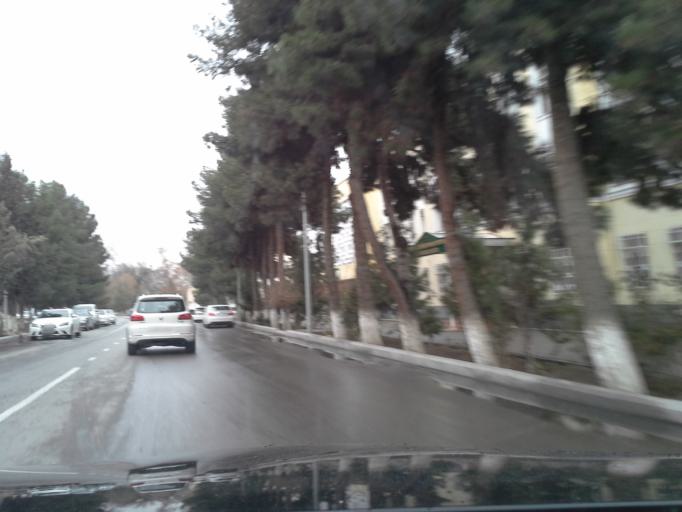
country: TM
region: Ahal
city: Ashgabat
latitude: 37.9553
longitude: 58.3659
